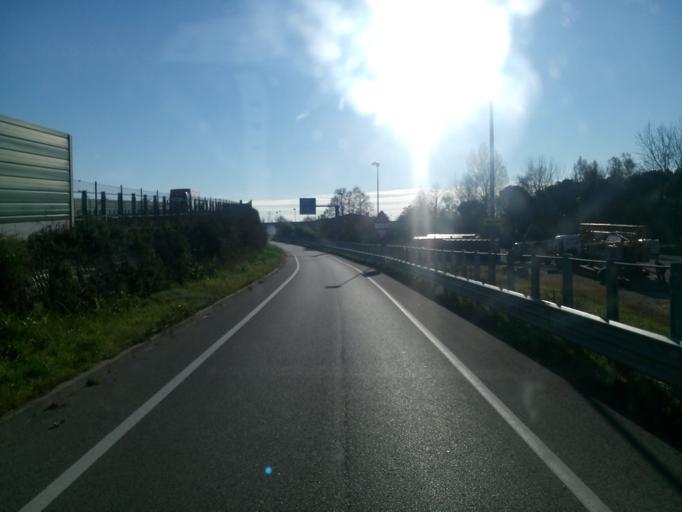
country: IT
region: Veneto
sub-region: Provincia di Padova
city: Loreggia
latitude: 45.6158
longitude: 11.9445
